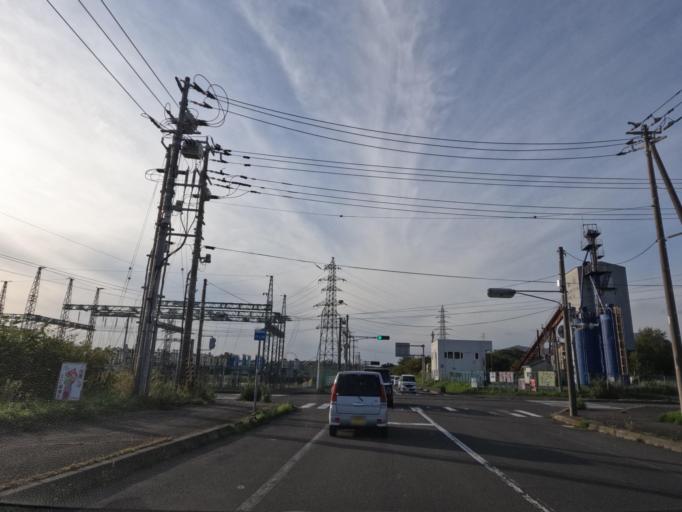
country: JP
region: Hokkaido
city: Date
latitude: 42.4852
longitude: 140.8771
